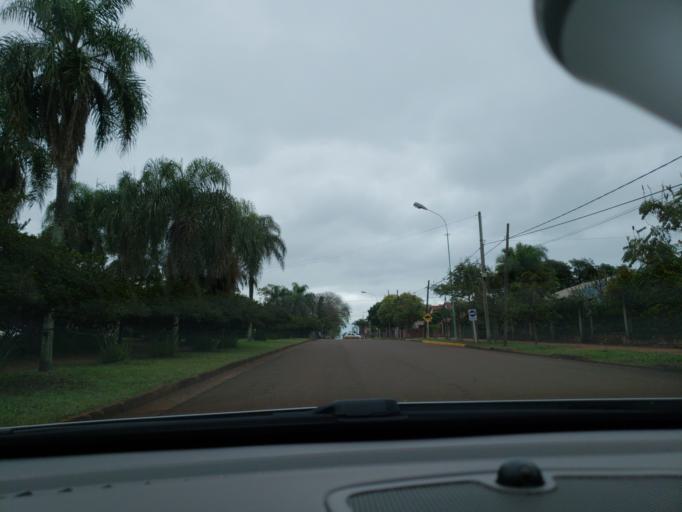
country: AR
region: Misiones
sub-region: Departamento de Apostoles
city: Apostoles
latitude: -27.9197
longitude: -55.7613
